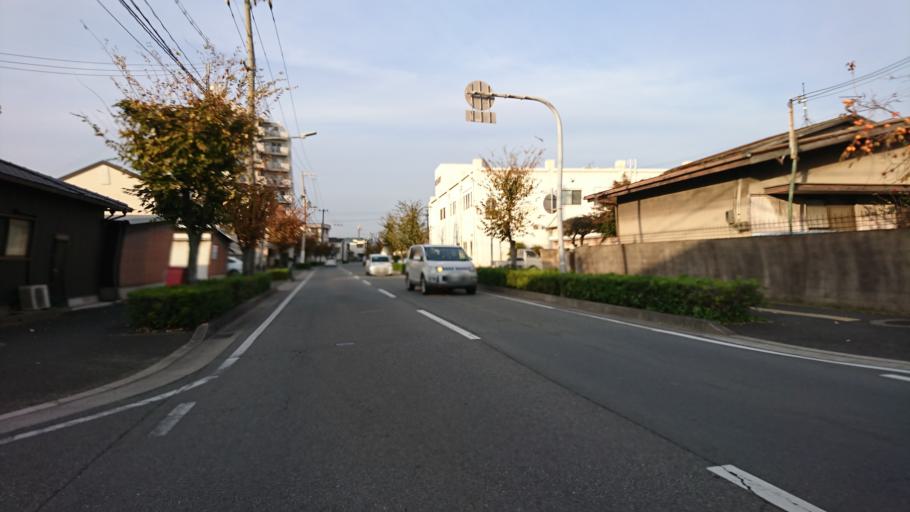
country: JP
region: Hyogo
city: Kakogawacho-honmachi
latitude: 34.7241
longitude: 134.8456
